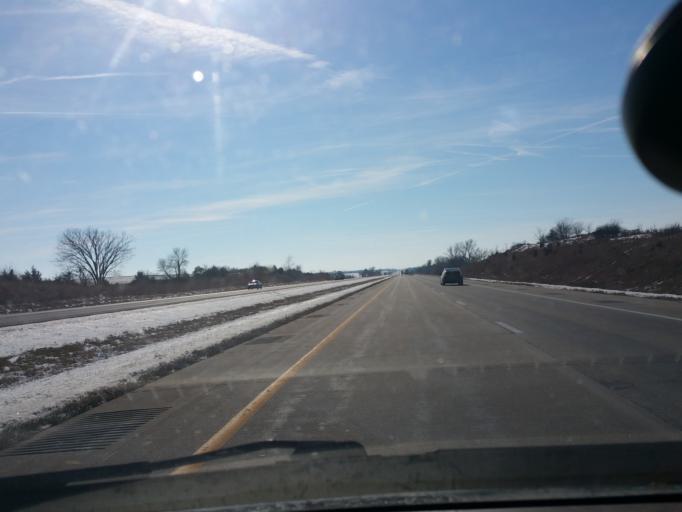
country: US
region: Missouri
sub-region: Harrison County
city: Bethany
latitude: 40.3405
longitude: -94.0113
